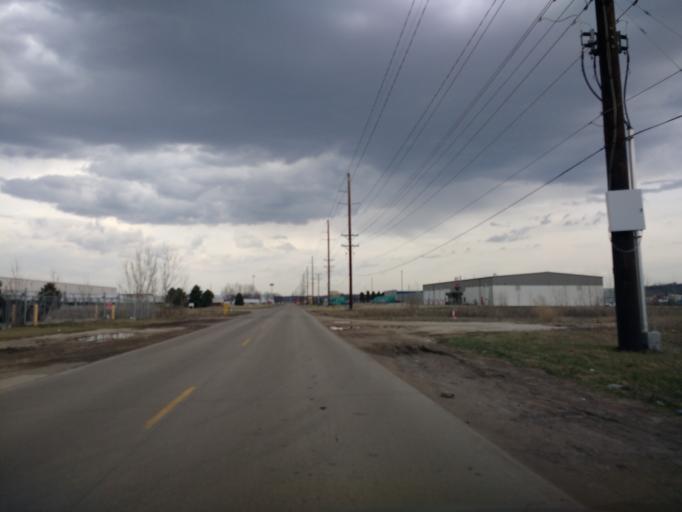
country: US
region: Iowa
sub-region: Woodbury County
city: Sergeant Bluff
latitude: 42.4174
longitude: -96.3699
